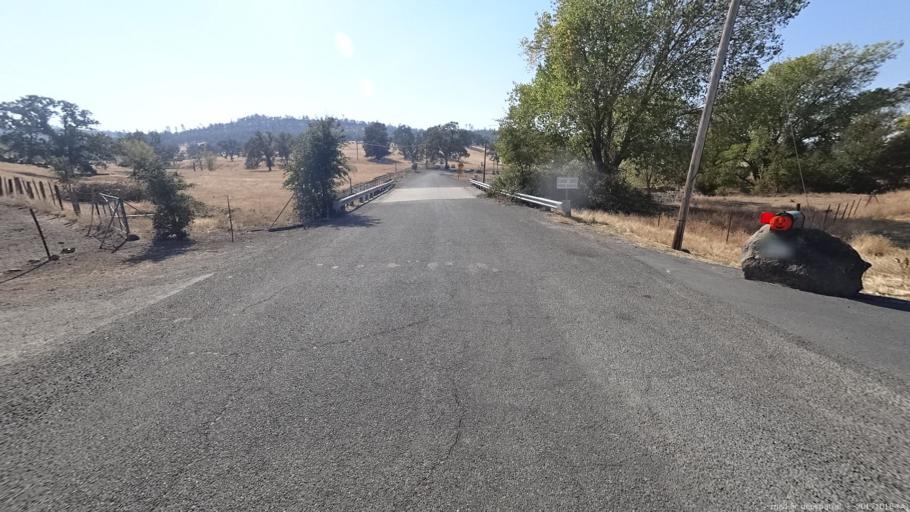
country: US
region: California
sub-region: Shasta County
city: Palo Cedro
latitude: 40.5485
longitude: -122.0773
